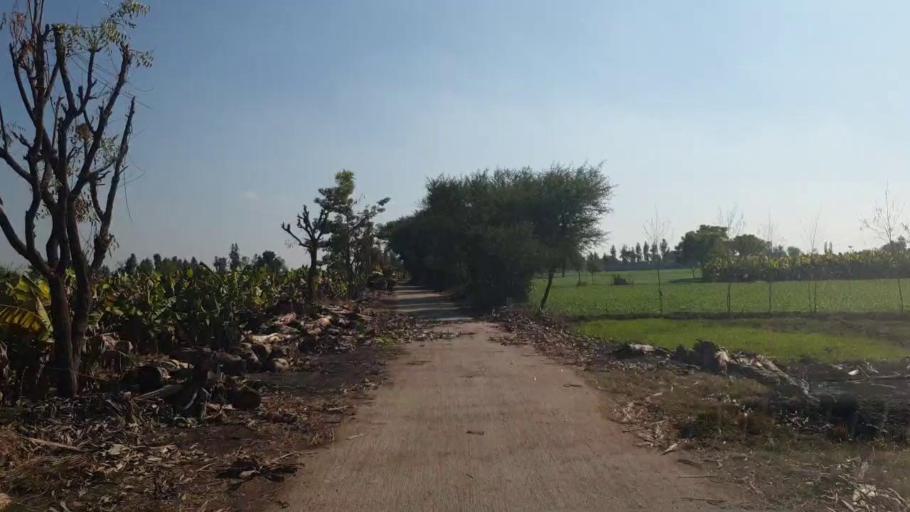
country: PK
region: Sindh
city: Shahdadpur
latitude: 25.9156
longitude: 68.5635
